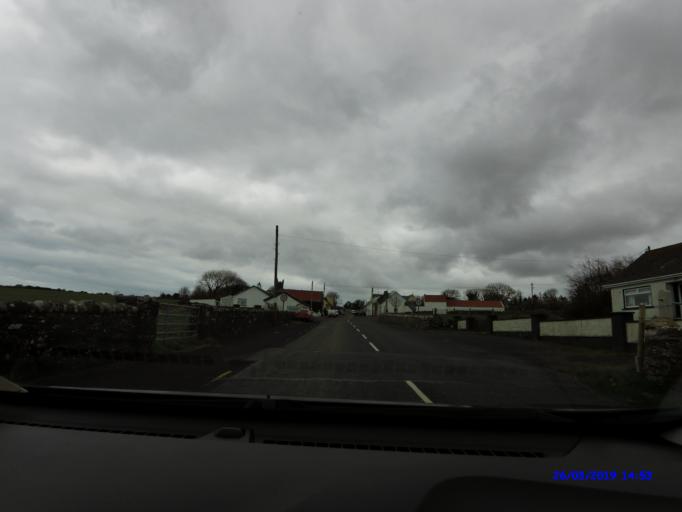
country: IE
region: Connaught
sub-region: Maigh Eo
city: Crossmolina
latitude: 54.2801
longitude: -9.3748
